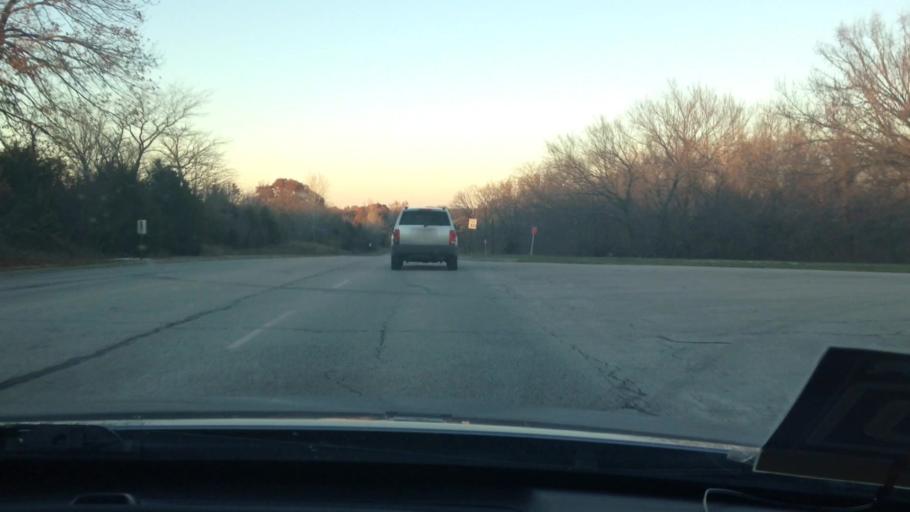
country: US
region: Kansas
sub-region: Wyandotte County
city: Bonner Springs
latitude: 39.1102
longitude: -94.8815
